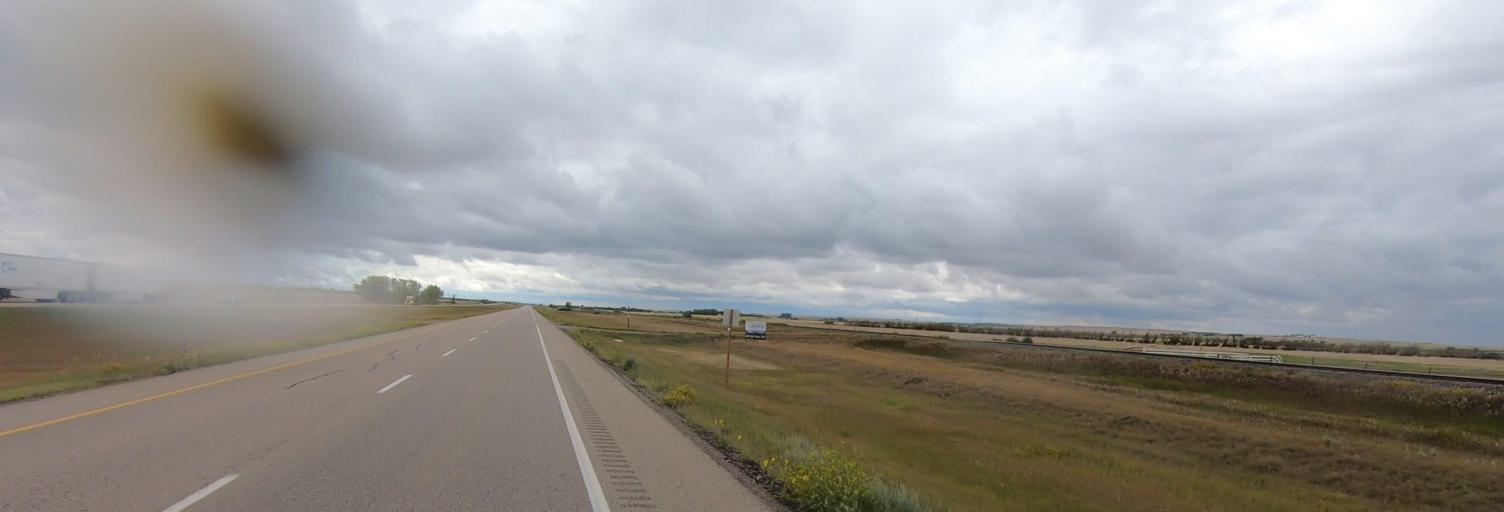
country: CA
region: Saskatchewan
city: Swift Current
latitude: 50.3714
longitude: -107.5330
